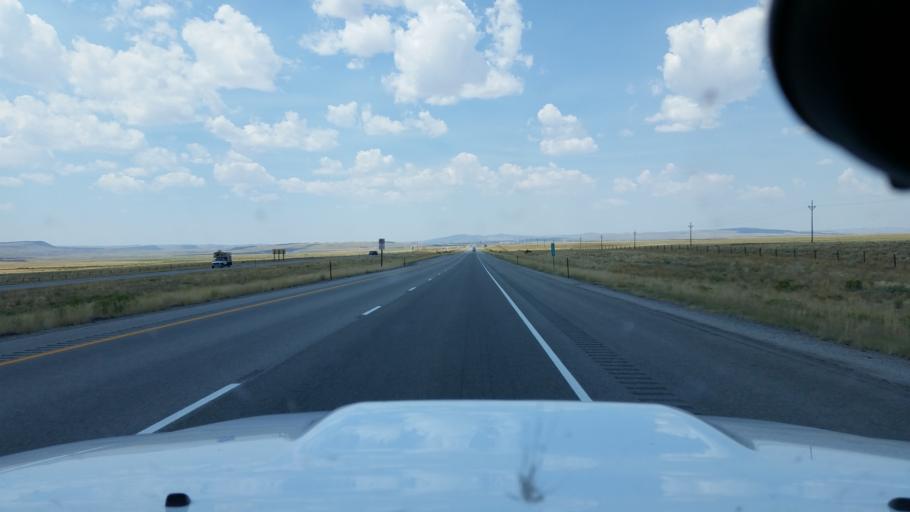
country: US
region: Wyoming
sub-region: Carbon County
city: Rawlins
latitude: 41.7587
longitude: -106.9854
